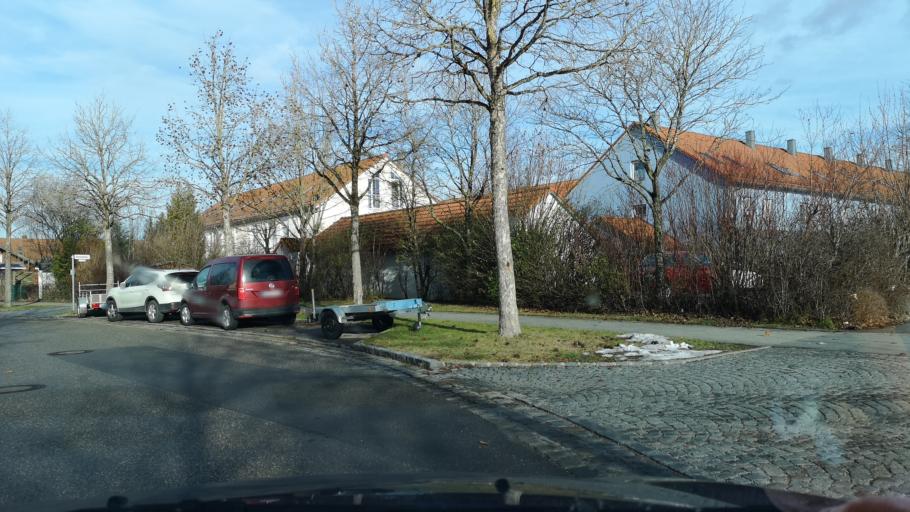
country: DE
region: Bavaria
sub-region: Upper Bavaria
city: Poing
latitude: 48.1762
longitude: 11.8092
